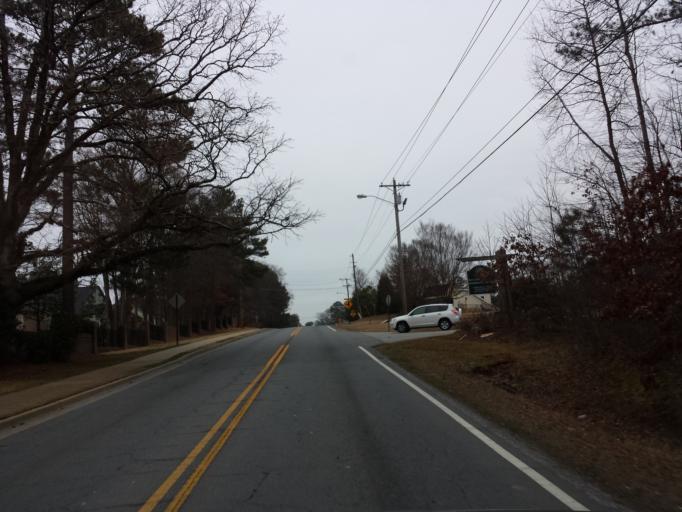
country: US
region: Georgia
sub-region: Fulton County
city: Roswell
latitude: 34.0153
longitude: -84.4330
